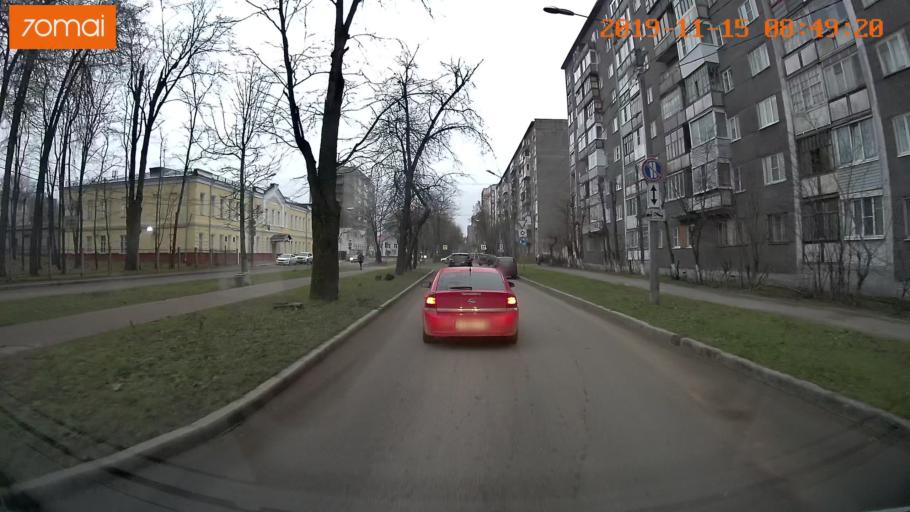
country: RU
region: Vologda
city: Cherepovets
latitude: 59.1231
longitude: 37.9217
